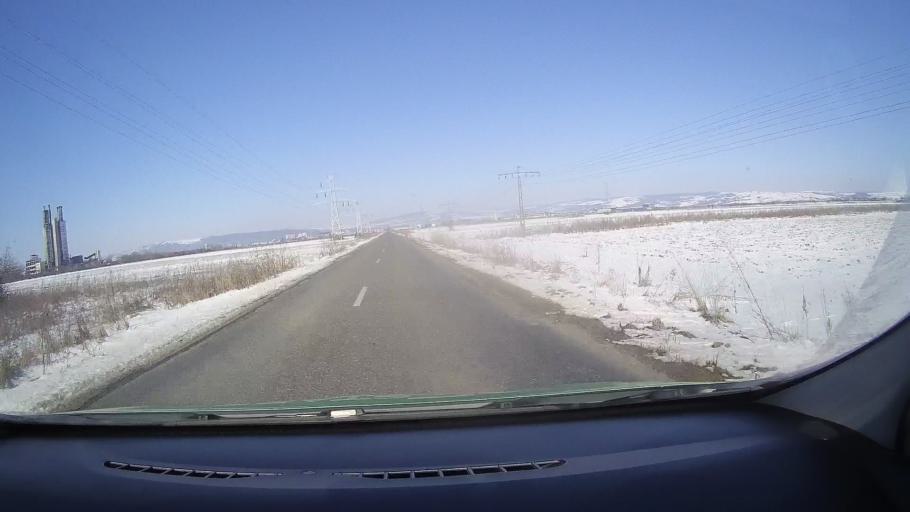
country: RO
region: Brasov
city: Fogarasch
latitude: 45.8107
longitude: 24.9895
